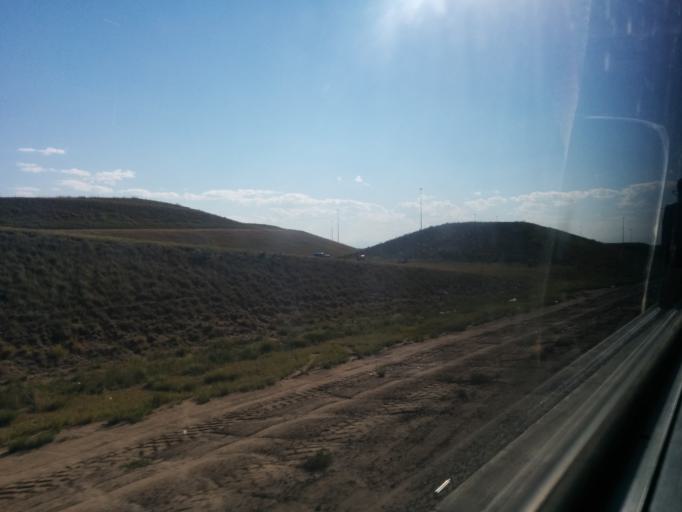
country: US
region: Colorado
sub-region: Adams County
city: Aurora
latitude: 39.8344
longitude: -104.7389
